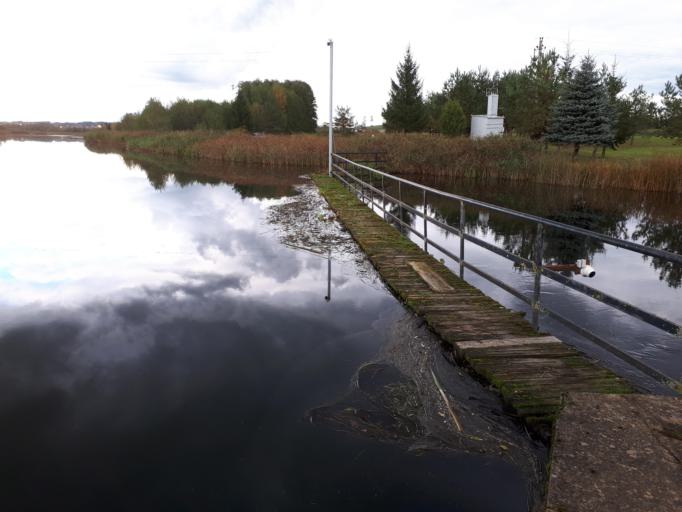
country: LT
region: Utenos apskritis
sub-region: Utena
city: Utena
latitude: 55.6461
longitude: 25.5817
